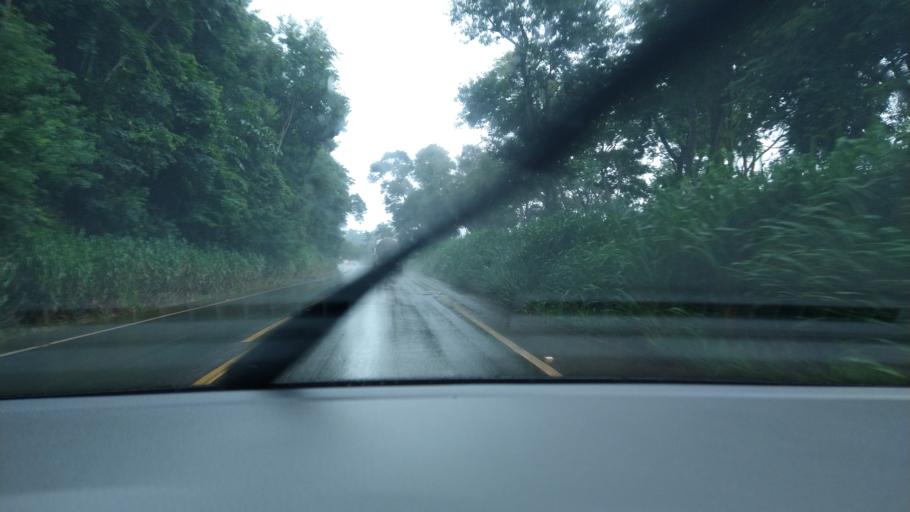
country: BR
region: Minas Gerais
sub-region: Vicosa
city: Vicosa
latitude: -20.5852
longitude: -42.8793
